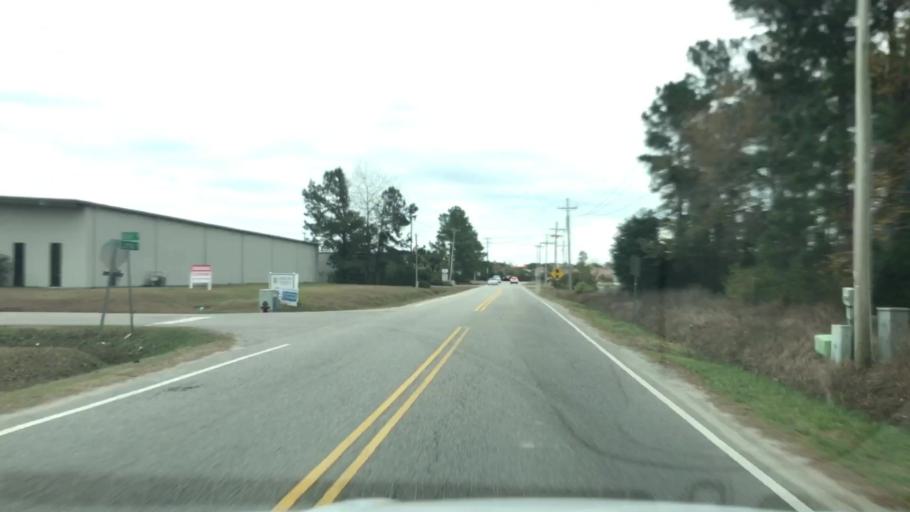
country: US
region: South Carolina
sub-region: Horry County
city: Forestbrook
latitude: 33.7158
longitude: -78.9397
